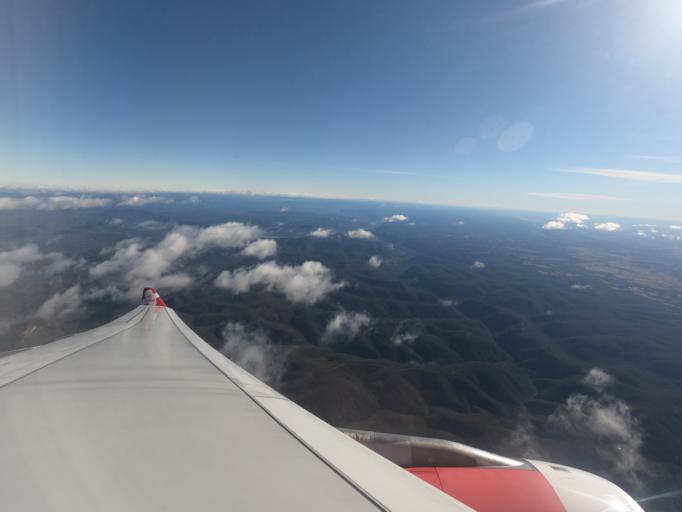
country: AU
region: New South Wales
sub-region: Wollondilly
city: Buxton
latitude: -34.2691
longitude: 150.4504
